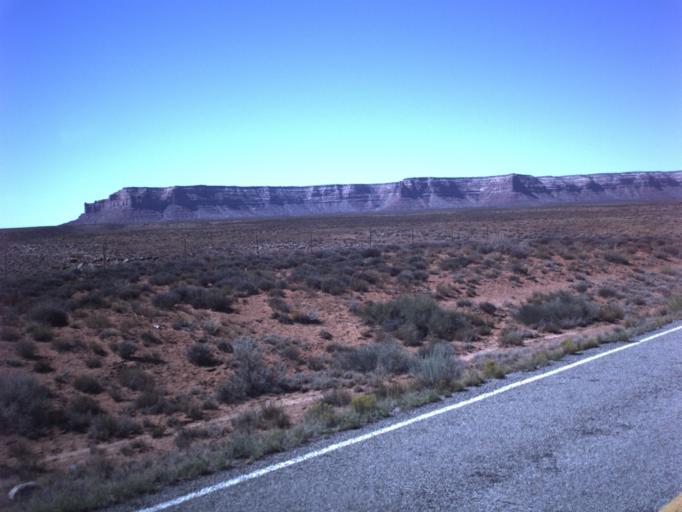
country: US
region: Utah
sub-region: San Juan County
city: Blanding
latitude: 37.2006
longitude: -109.8799
